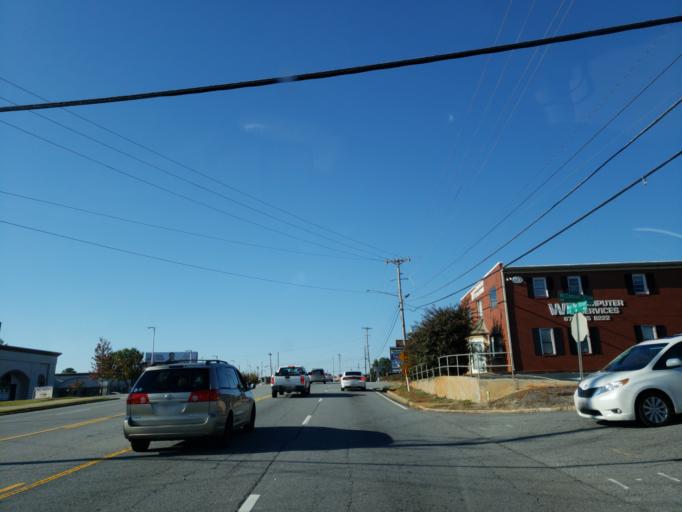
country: US
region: Georgia
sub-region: Gwinnett County
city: Lawrenceville
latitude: 33.9634
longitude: -84.0071
